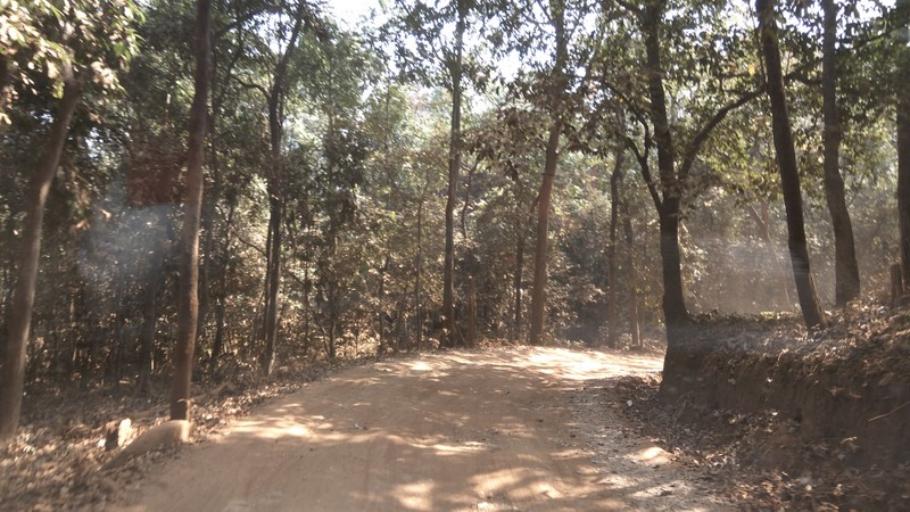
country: IN
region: Goa
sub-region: South Goa
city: Sanguem
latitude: 15.3260
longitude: 74.2834
